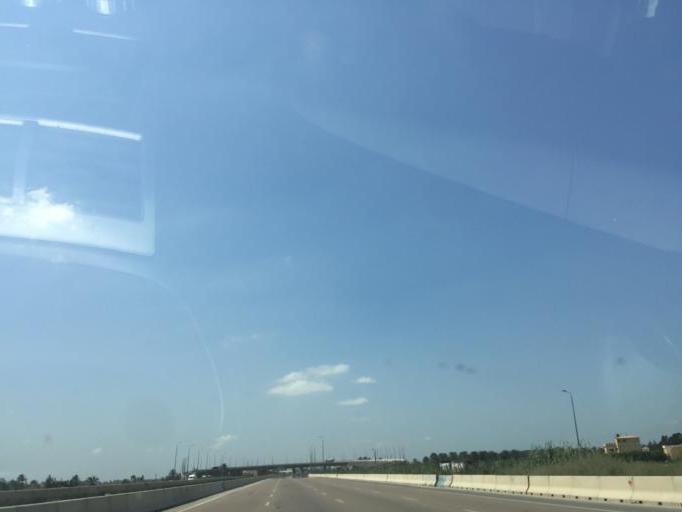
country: EG
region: Al Buhayrah
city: Abu al Matamir
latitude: 30.8836
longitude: 29.8828
